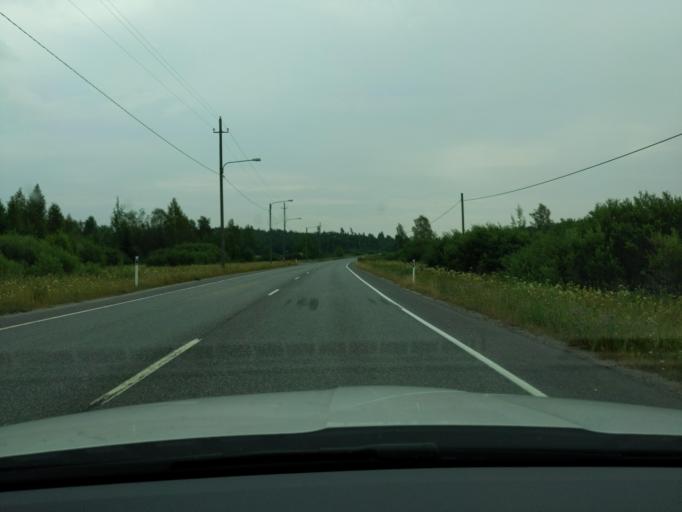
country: FI
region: Uusimaa
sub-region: Helsinki
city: Pornainen
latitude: 60.3447
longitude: 25.4534
